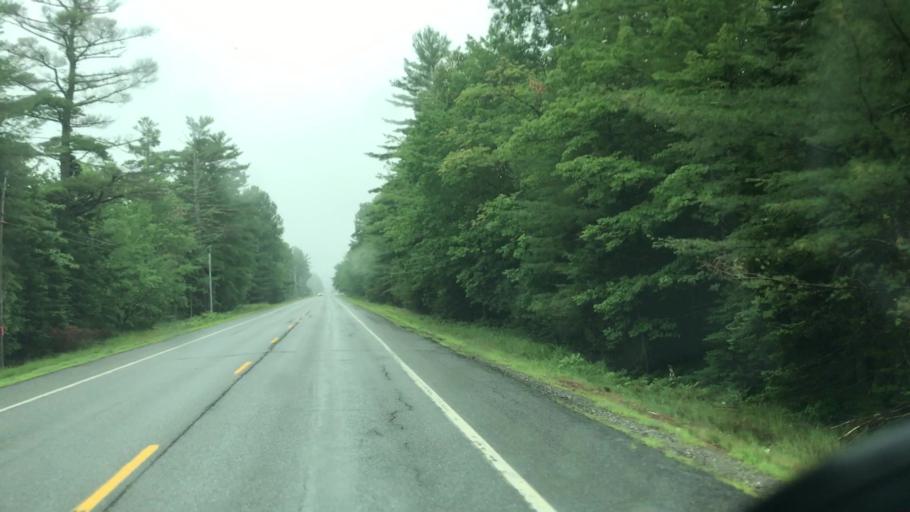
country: US
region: Maine
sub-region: Penobscot County
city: Howland
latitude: 45.2455
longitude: -68.6400
